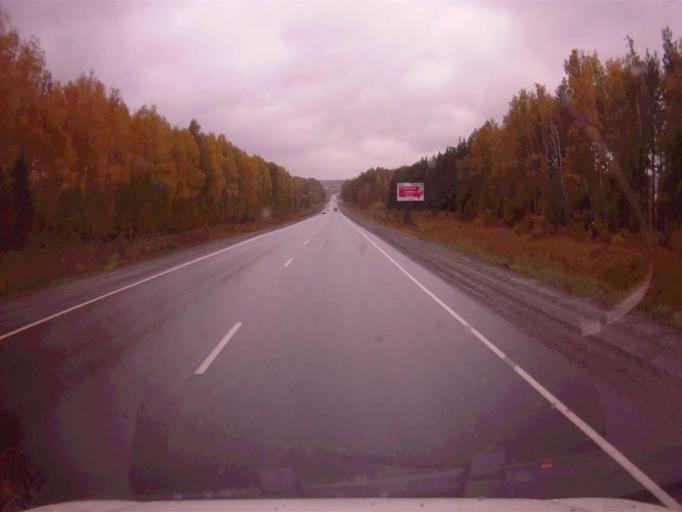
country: RU
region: Chelyabinsk
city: Roshchino
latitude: 55.3626
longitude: 61.2122
